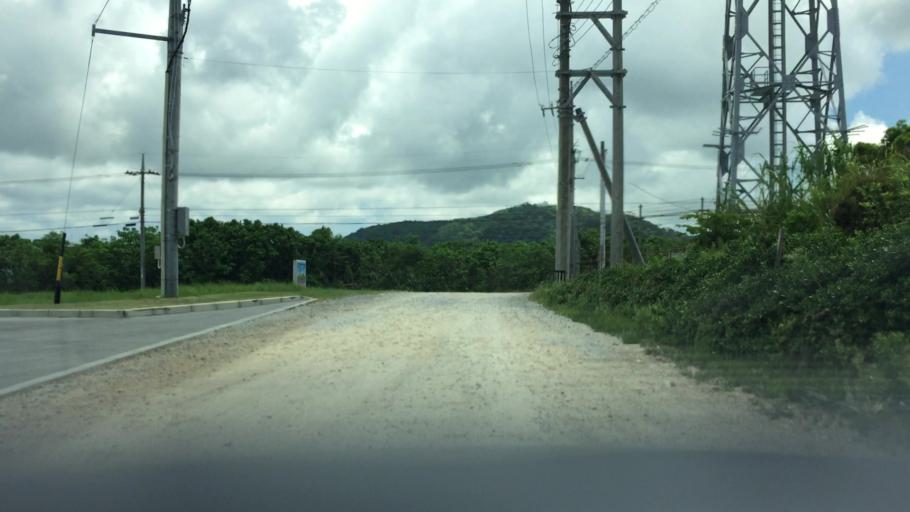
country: JP
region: Okinawa
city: Ishigaki
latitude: 24.3711
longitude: 124.1231
